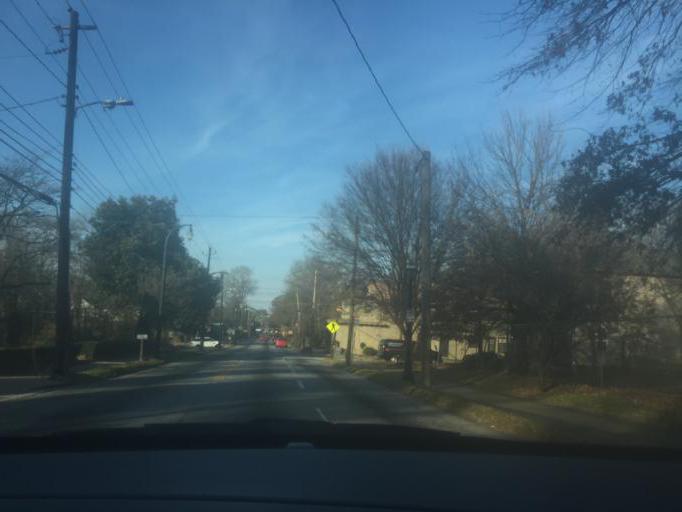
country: US
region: Georgia
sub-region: Fulton County
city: Atlanta
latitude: 33.7502
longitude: -84.4175
